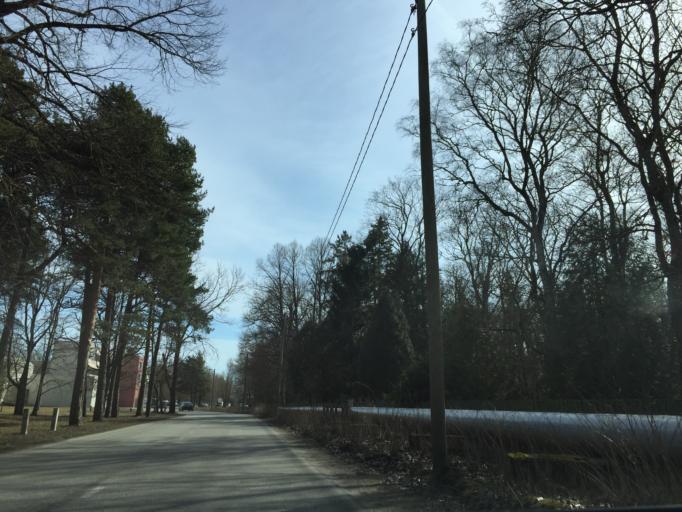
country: EE
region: Paernumaa
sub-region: Paernu linn
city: Parnu
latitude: 58.3789
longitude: 24.5354
